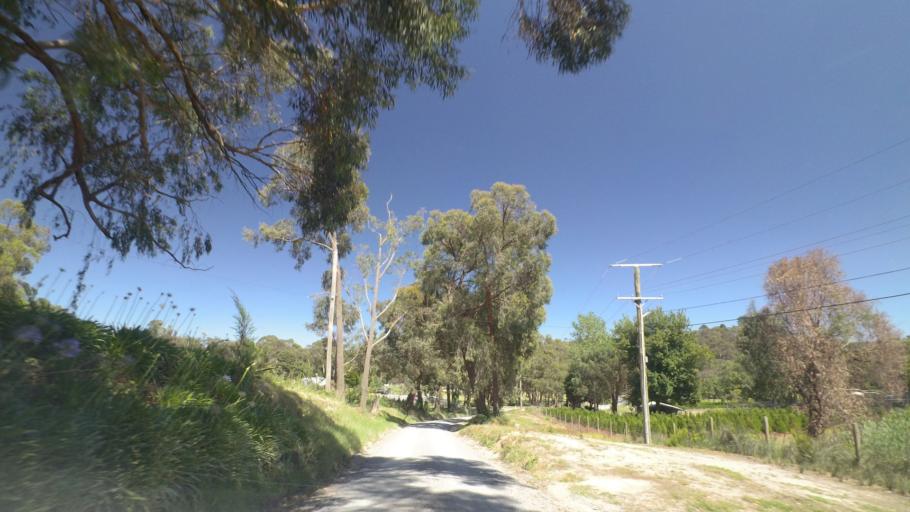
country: AU
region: Victoria
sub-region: Yarra Ranges
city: Kalorama
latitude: -37.8029
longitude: 145.3614
